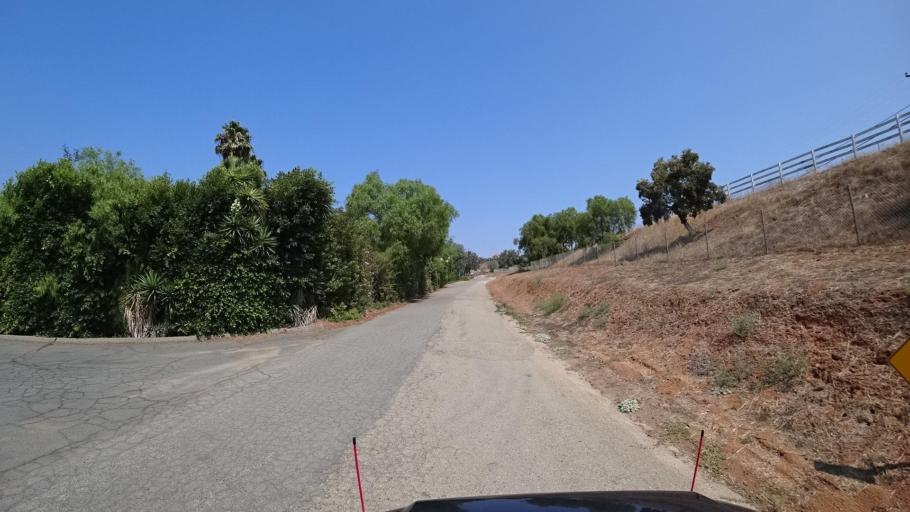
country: US
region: California
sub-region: San Diego County
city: Bonsall
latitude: 33.2763
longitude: -117.2454
